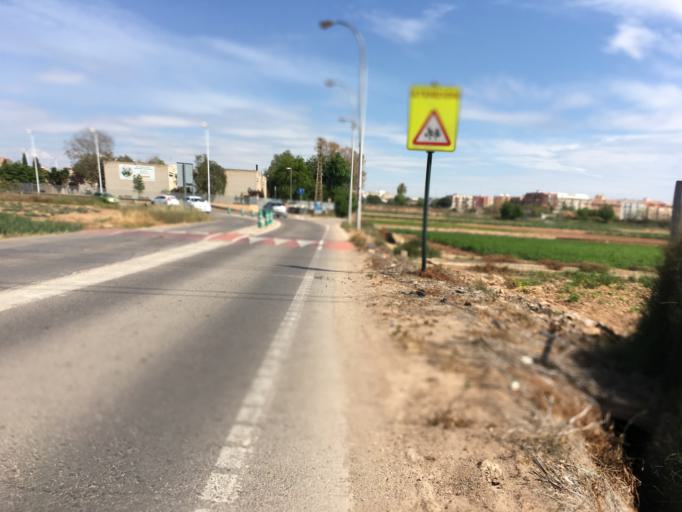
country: ES
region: Valencia
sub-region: Provincia de Valencia
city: Paterna
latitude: 39.4929
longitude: -0.4181
